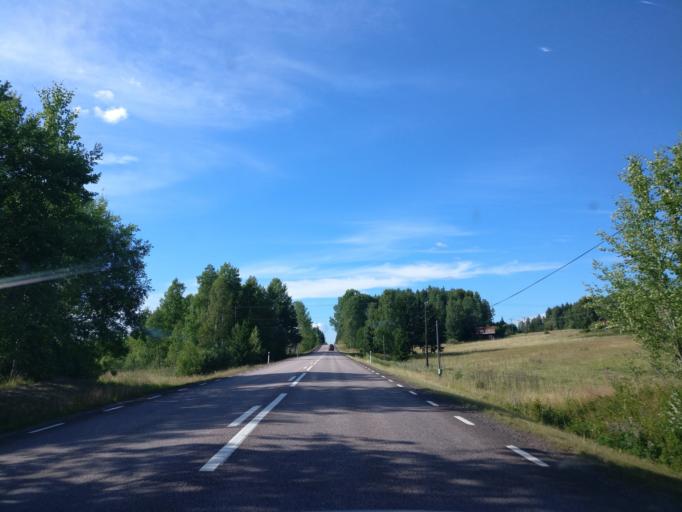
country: SE
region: Vaermland
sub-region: Karlstads Kommun
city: Edsvalla
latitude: 59.5812
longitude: 13.0164
